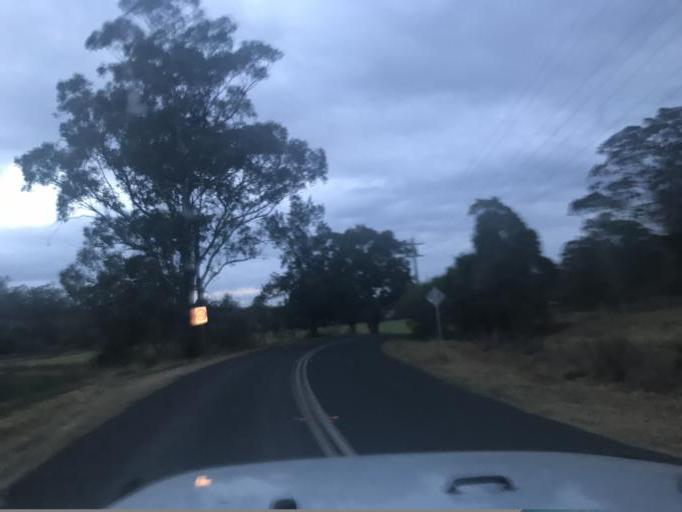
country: AU
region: New South Wales
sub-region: Hawkesbury
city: Pitt Town
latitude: -33.5031
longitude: 150.8760
